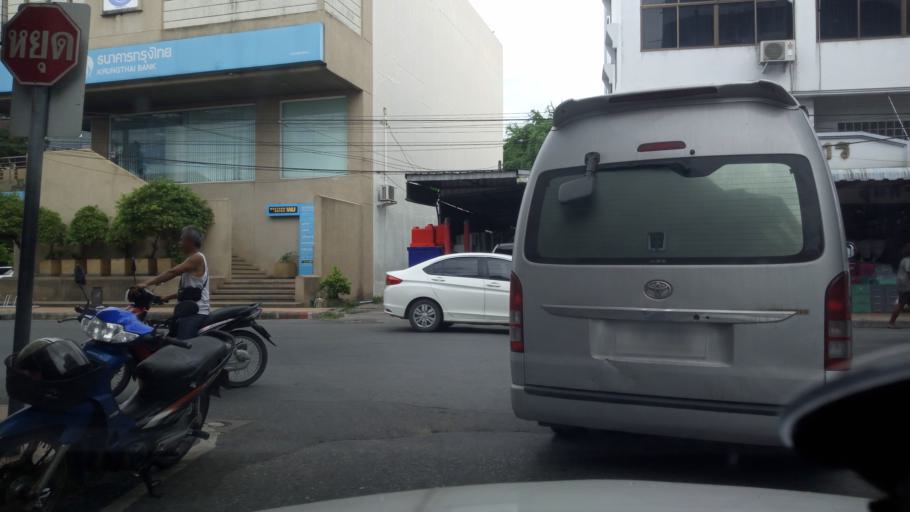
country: TH
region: Chon Buri
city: Phanat Nikhom
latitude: 13.4527
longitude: 101.1816
